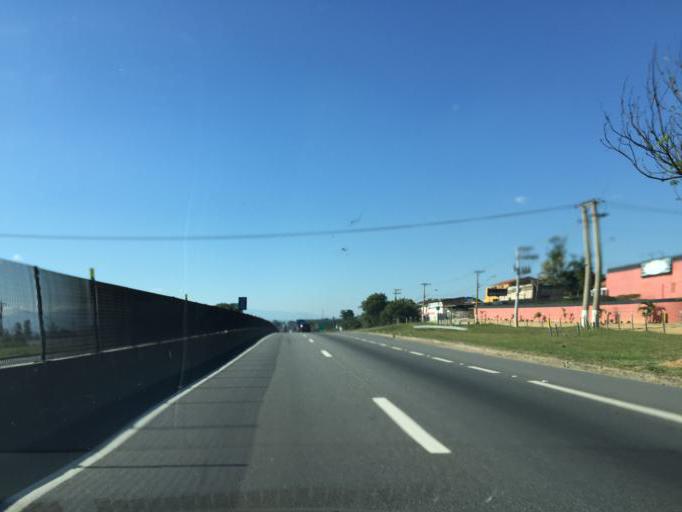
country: BR
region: Sao Paulo
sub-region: Guaratingueta
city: Guaratingueta
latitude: -22.7855
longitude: -45.1534
